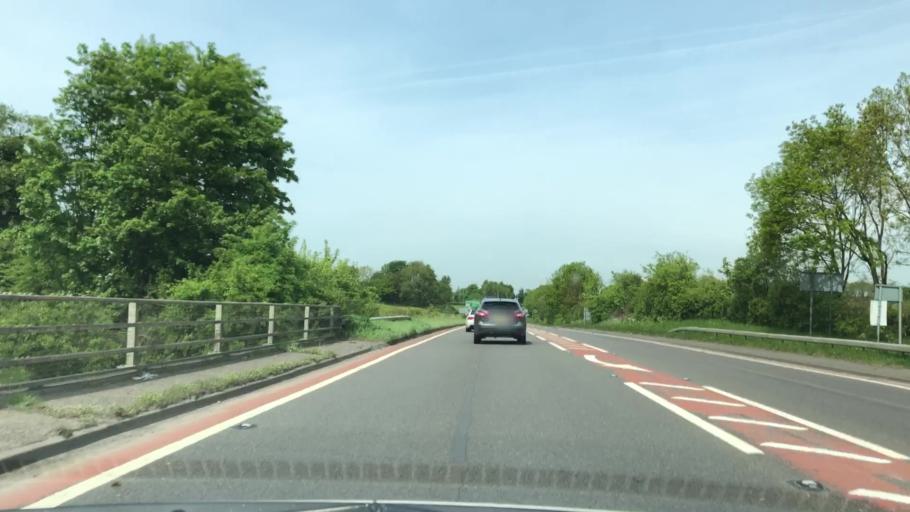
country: GB
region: England
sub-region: Shropshire
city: Gobowen
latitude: 52.9142
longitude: -3.0426
